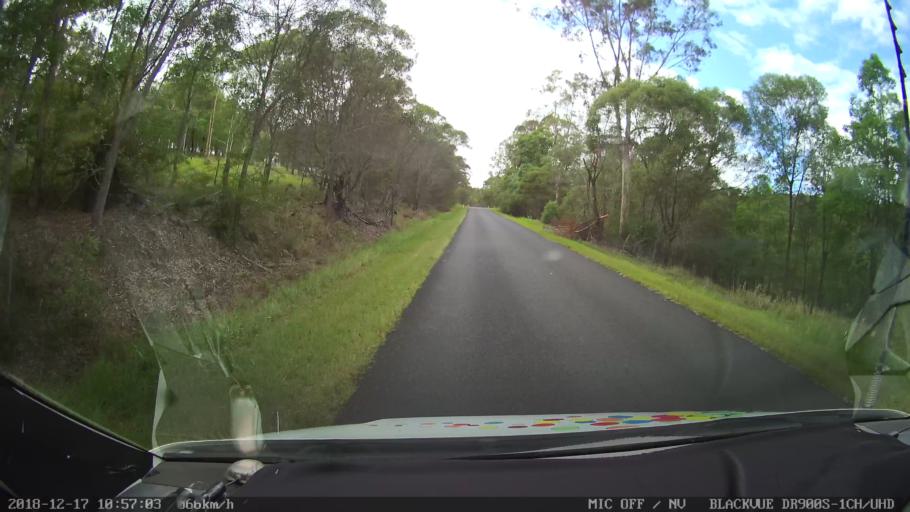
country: AU
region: New South Wales
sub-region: Richmond Valley
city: Casino
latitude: -28.8235
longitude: 152.5934
